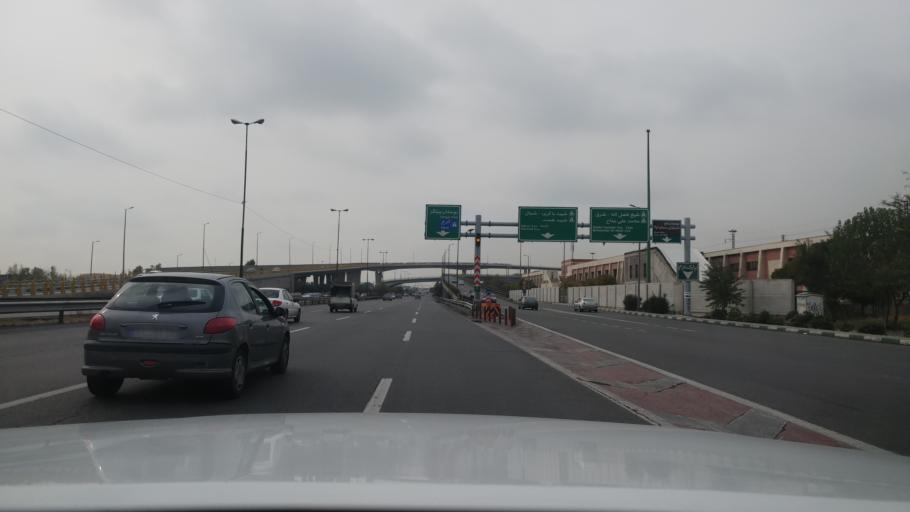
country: IR
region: Tehran
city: Tehran
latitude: 35.7171
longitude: 51.3042
